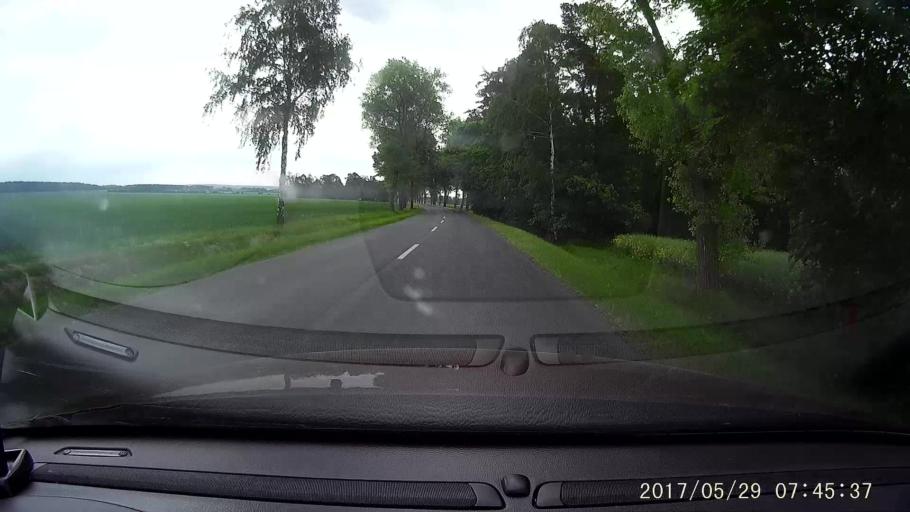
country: PL
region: Lower Silesian Voivodeship
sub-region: Powiat boleslawiecki
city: Boleslawiec
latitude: 51.2368
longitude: 15.6302
